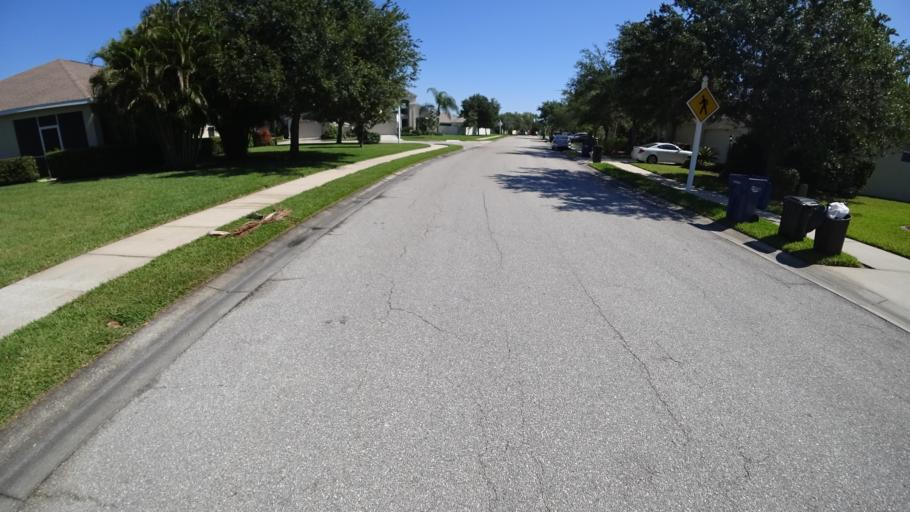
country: US
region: Florida
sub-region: Manatee County
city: Ellenton
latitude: 27.5637
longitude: -82.4433
